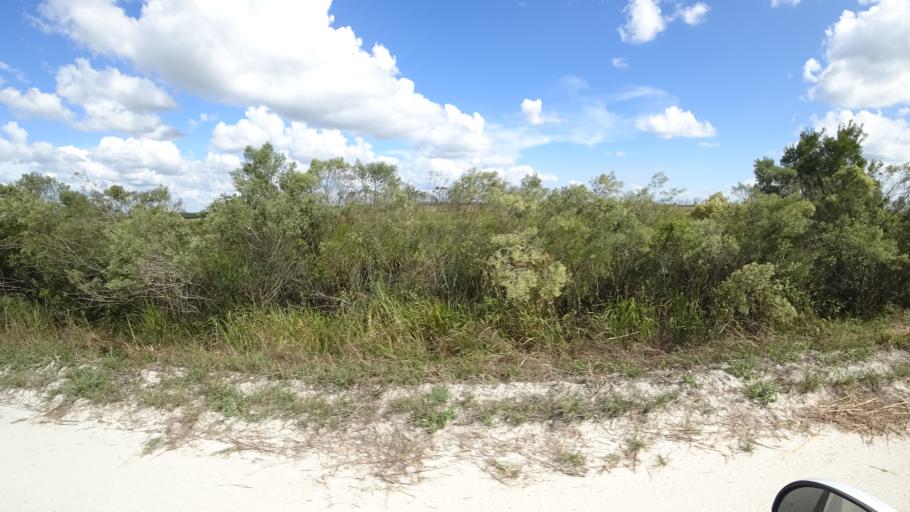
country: US
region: Florida
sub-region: DeSoto County
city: Arcadia
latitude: 27.3237
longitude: -82.1050
